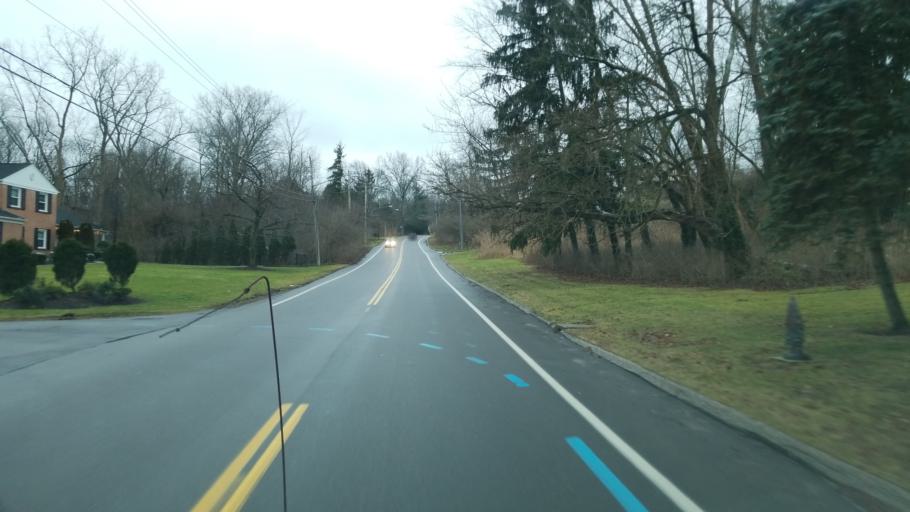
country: US
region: Ohio
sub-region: Summit County
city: Akron
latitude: 41.1215
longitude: -81.5482
